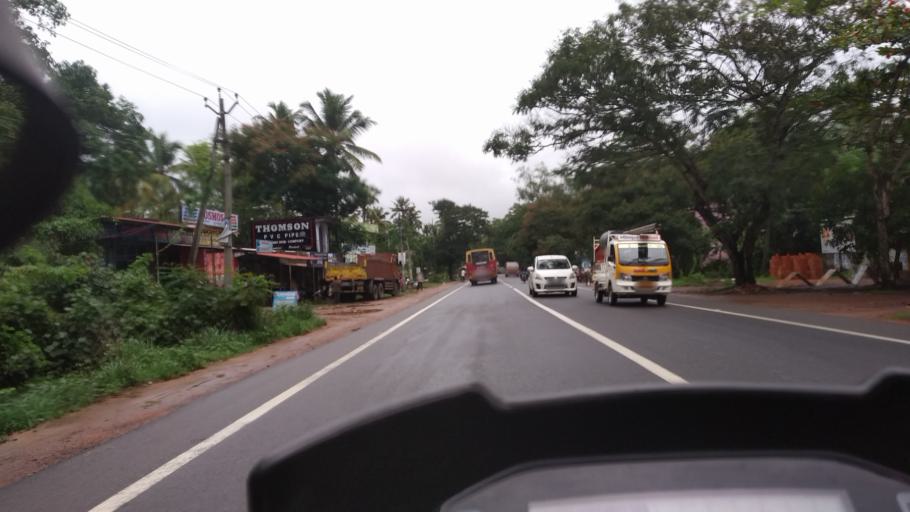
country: IN
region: Kerala
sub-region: Alappuzha
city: Mavelikara
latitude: 9.2857
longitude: 76.4395
